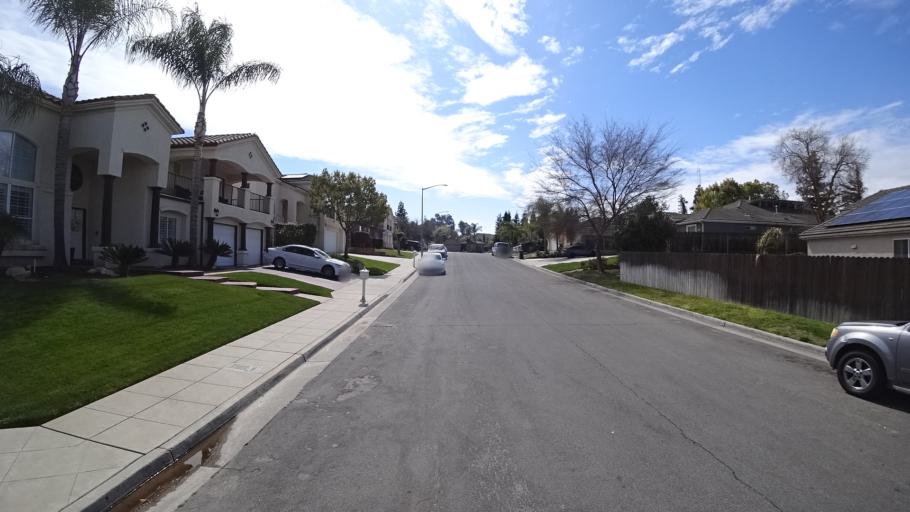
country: US
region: California
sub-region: Fresno County
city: Biola
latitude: 36.8490
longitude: -119.9011
